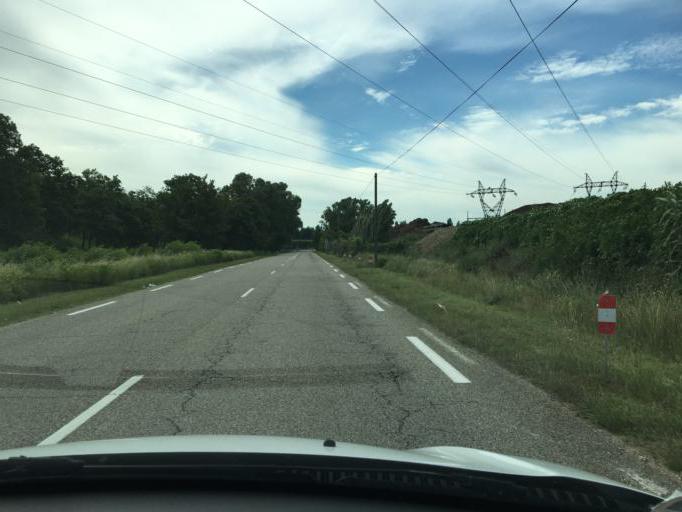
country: FR
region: Provence-Alpes-Cote d'Azur
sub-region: Departement du Vaucluse
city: Bollene
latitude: 44.3067
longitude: 4.7369
